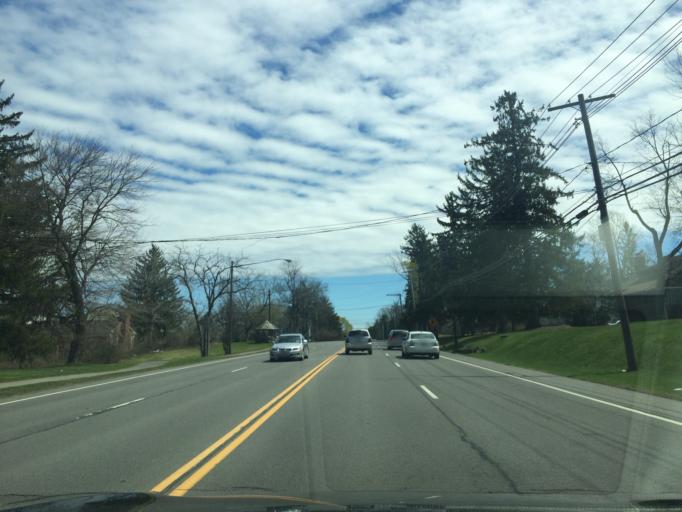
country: US
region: New York
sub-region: Monroe County
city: Pittsford
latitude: 43.0991
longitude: -77.5331
